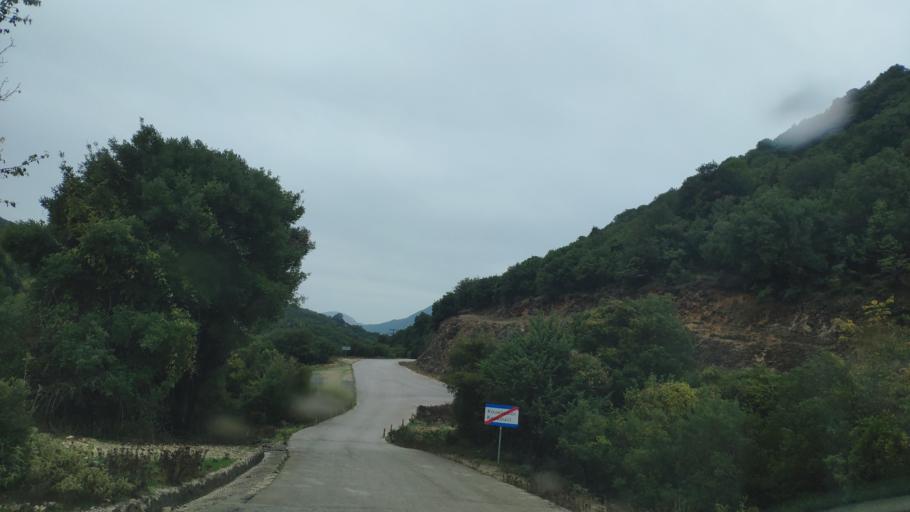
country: GR
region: Epirus
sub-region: Nomos Thesprotias
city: Paramythia
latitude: 39.4311
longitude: 20.6251
